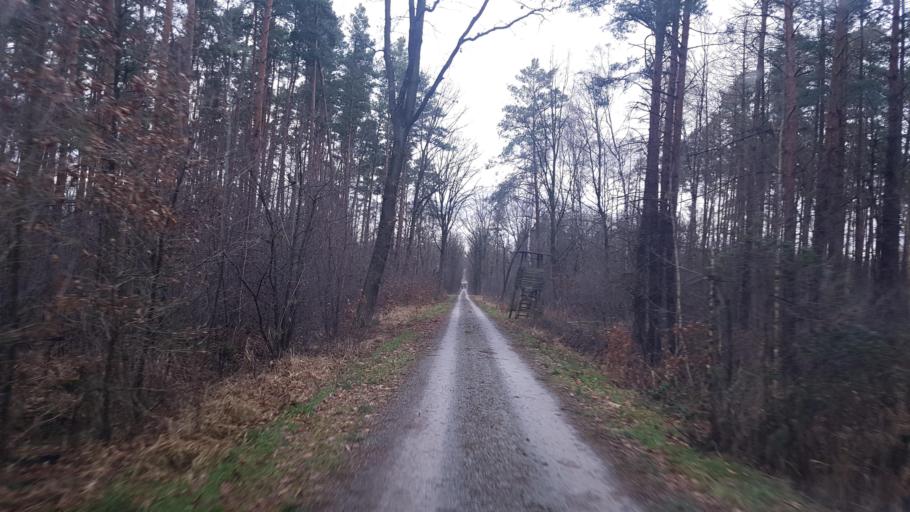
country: DE
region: Brandenburg
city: Plessa
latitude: 51.4411
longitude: 13.6510
